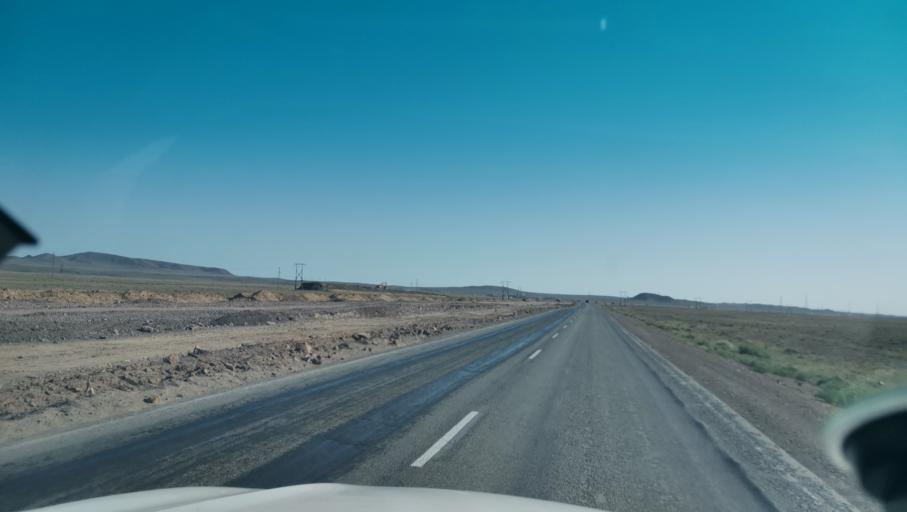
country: KZ
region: Qaraghandy
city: Balqash
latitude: 46.6631
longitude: 74.4071
